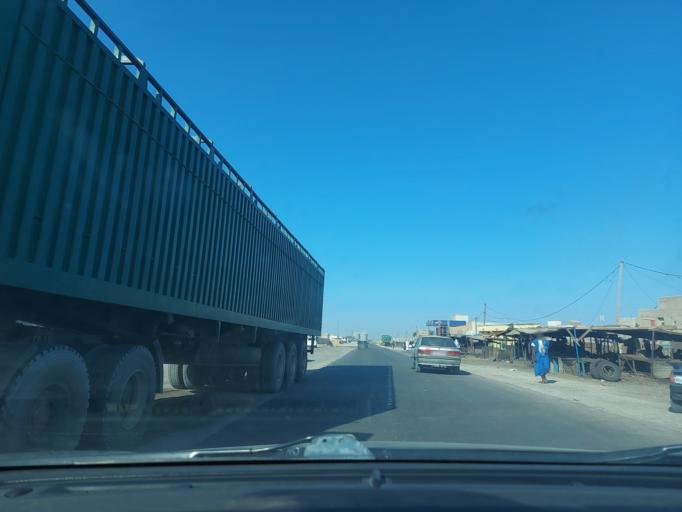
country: MR
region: Nouakchott
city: Nouakchott
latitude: 18.0529
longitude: -15.9843
